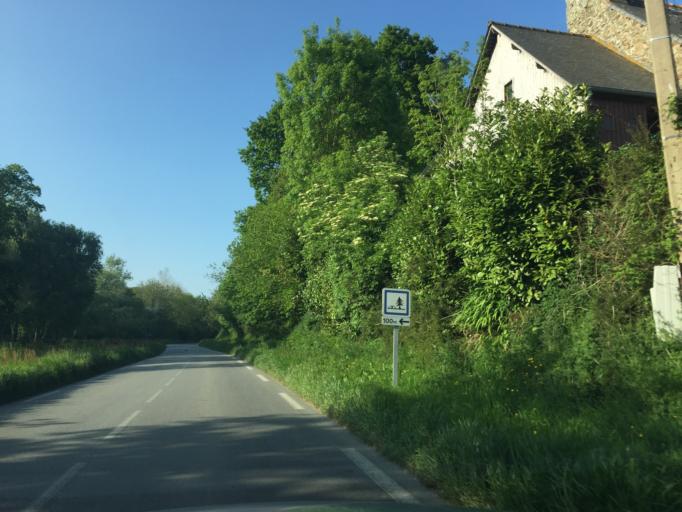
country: FR
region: Brittany
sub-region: Departement des Cotes-d'Armor
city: Crehen
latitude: 48.5692
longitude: -2.2410
